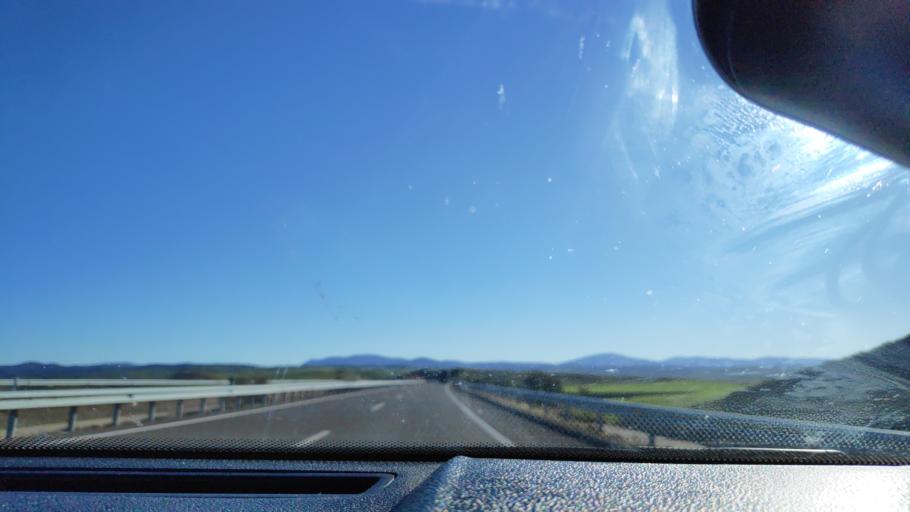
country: ES
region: Extremadura
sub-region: Provincia de Badajoz
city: Fuente de Cantos
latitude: 38.1856
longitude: -6.2793
